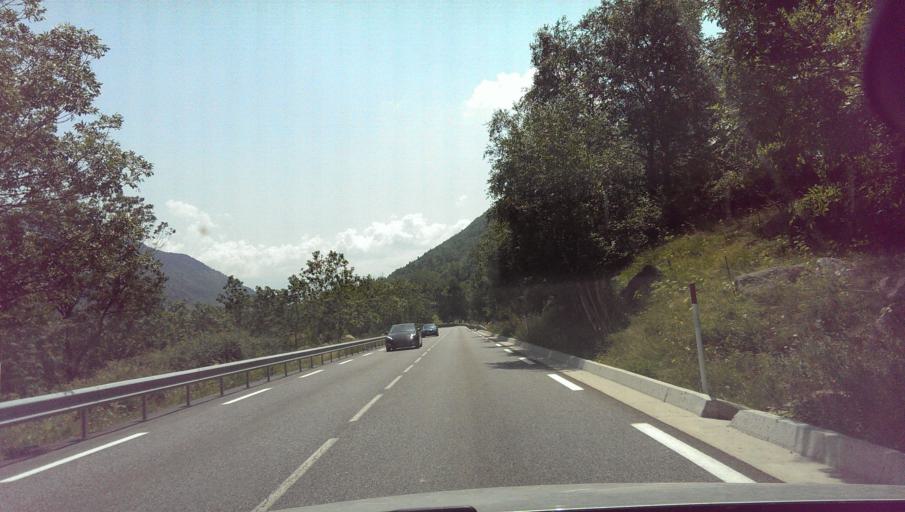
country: ES
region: Catalonia
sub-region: Provincia de Girona
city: Guils de Cerdanya
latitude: 42.5005
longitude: 1.8377
